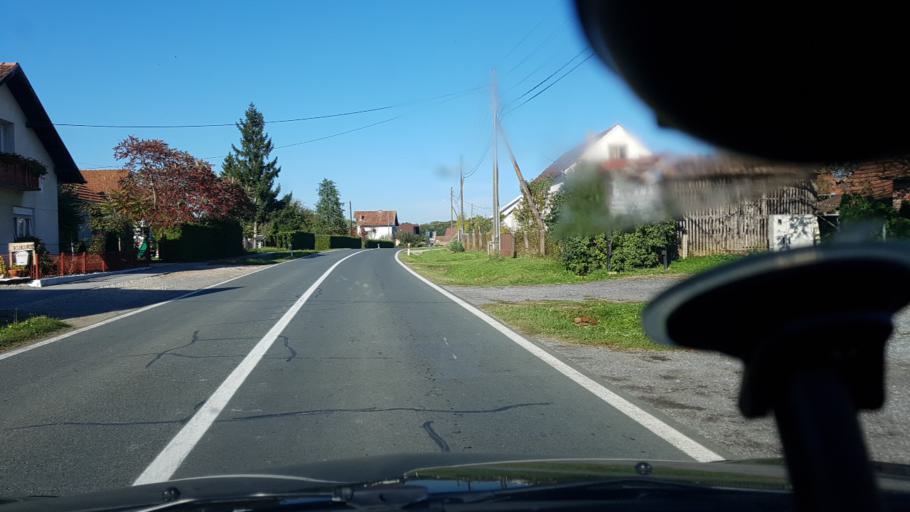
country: HR
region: Bjelovarsko-Bilogorska
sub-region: Grad Cazma
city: Cazma
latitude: 45.7777
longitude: 16.6390
